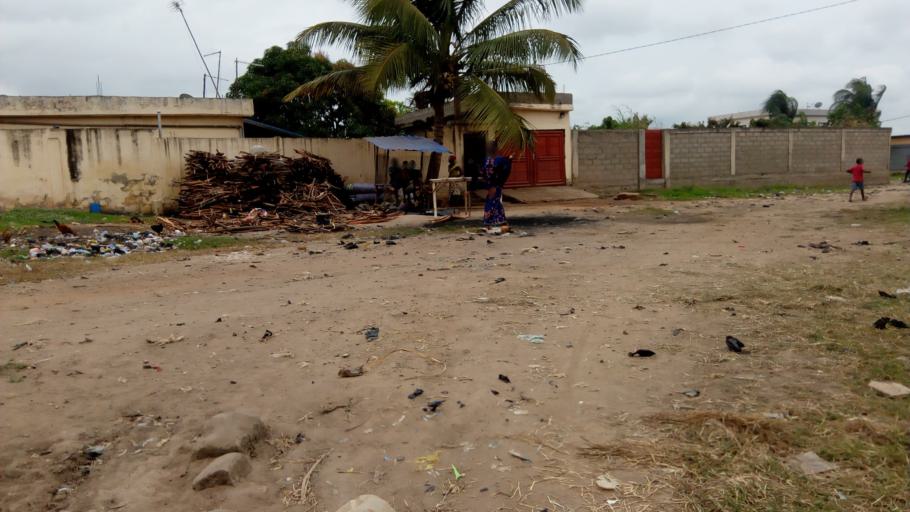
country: TG
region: Maritime
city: Lome
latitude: 6.2532
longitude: 1.2185
